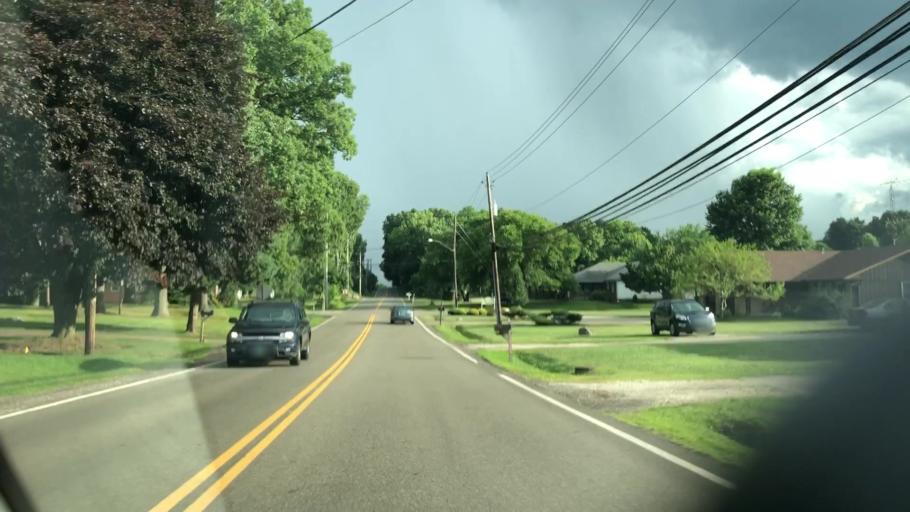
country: US
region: Ohio
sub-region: Stark County
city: North Canton
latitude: 40.8588
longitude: -81.4423
